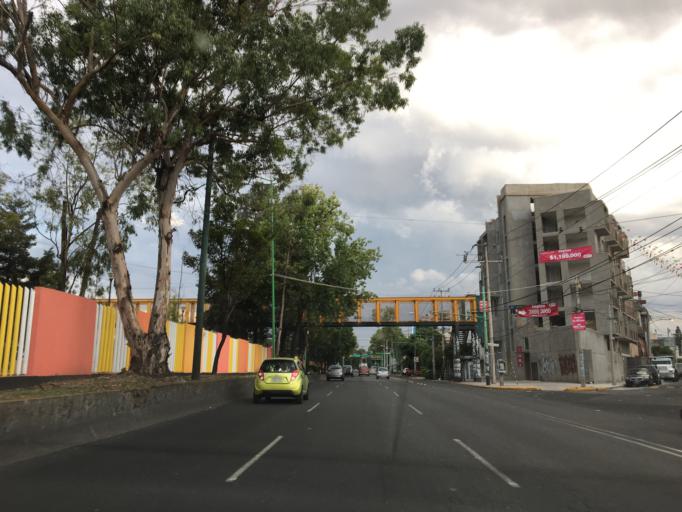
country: MX
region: Mexico
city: Colonia Lindavista
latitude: 19.4738
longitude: -99.1389
